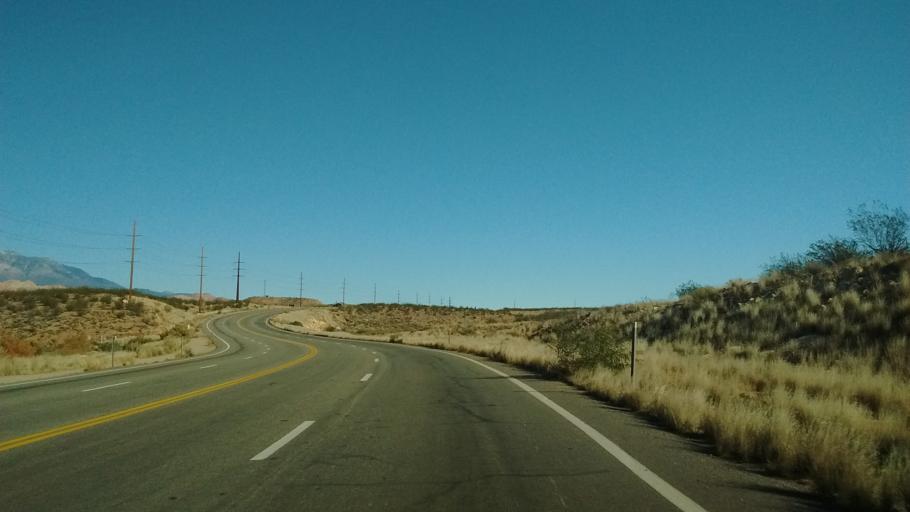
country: US
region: Utah
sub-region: Washington County
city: Washington
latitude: 37.1485
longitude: -113.4487
